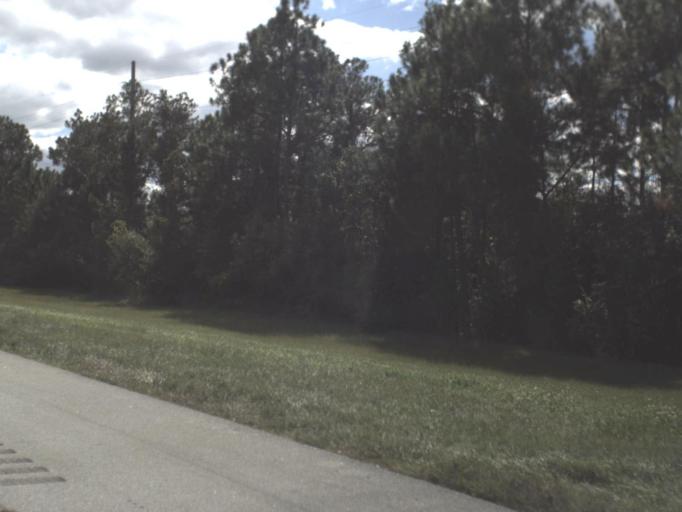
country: US
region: Florida
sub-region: Osceola County
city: Buenaventura Lakes
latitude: 28.3134
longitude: -81.3694
